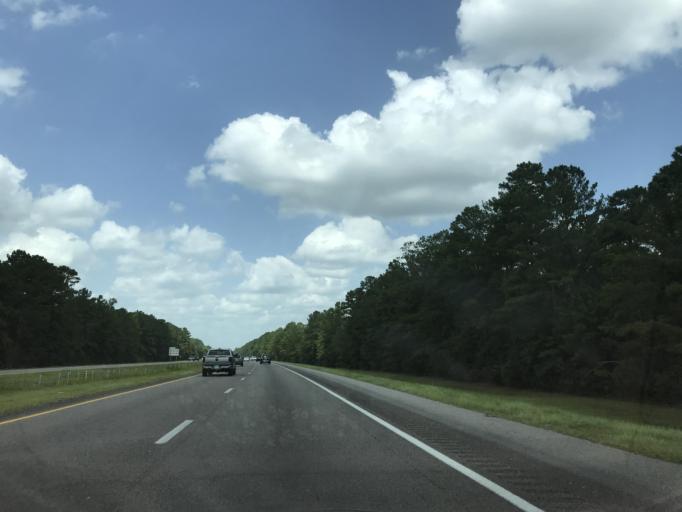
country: US
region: North Carolina
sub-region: Pender County
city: Burgaw
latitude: 34.5876
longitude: -77.9058
